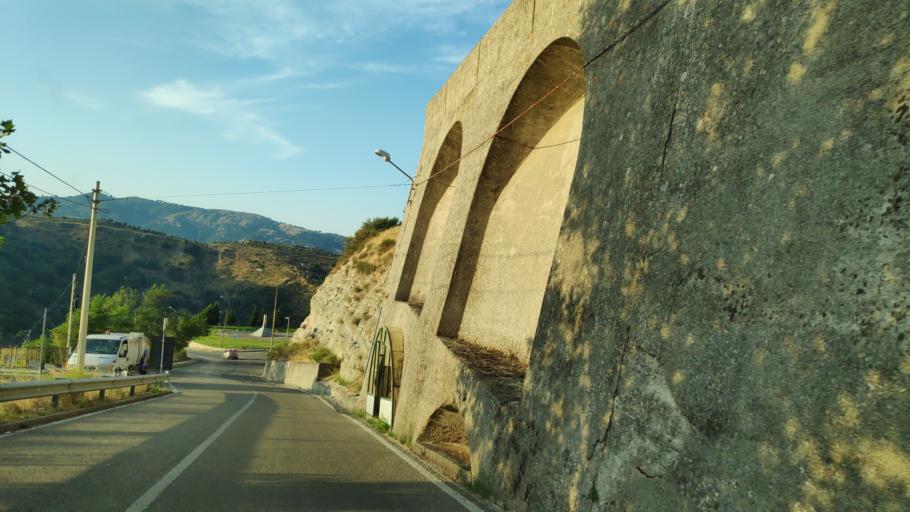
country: IT
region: Calabria
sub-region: Provincia di Catanzaro
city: Satriano
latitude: 38.6688
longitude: 16.4812
